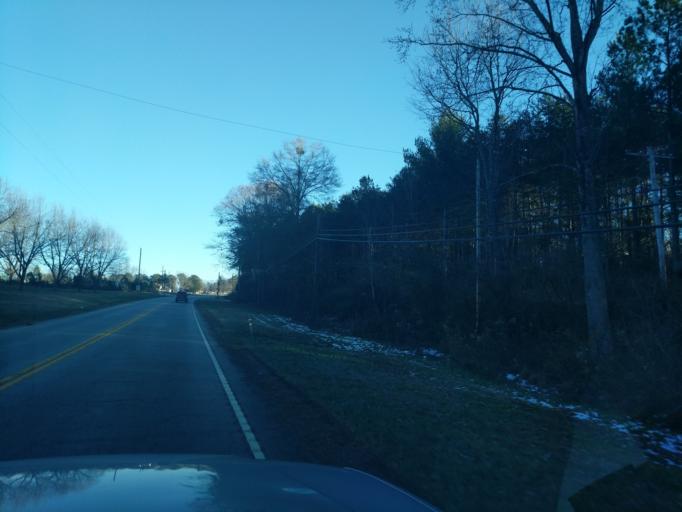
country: US
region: South Carolina
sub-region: Oconee County
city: Westminster
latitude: 34.6812
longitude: -83.1213
